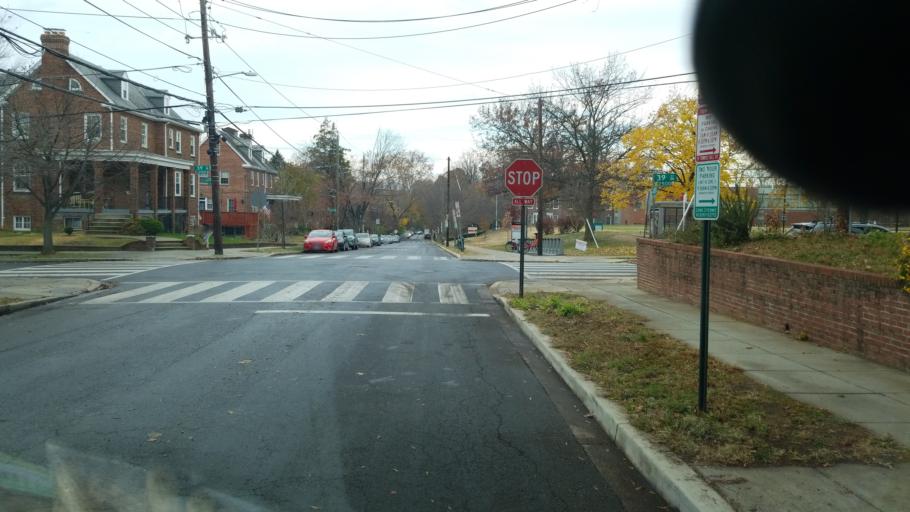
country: US
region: Maryland
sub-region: Montgomery County
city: Friendship Village
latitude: 38.9226
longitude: -77.0767
